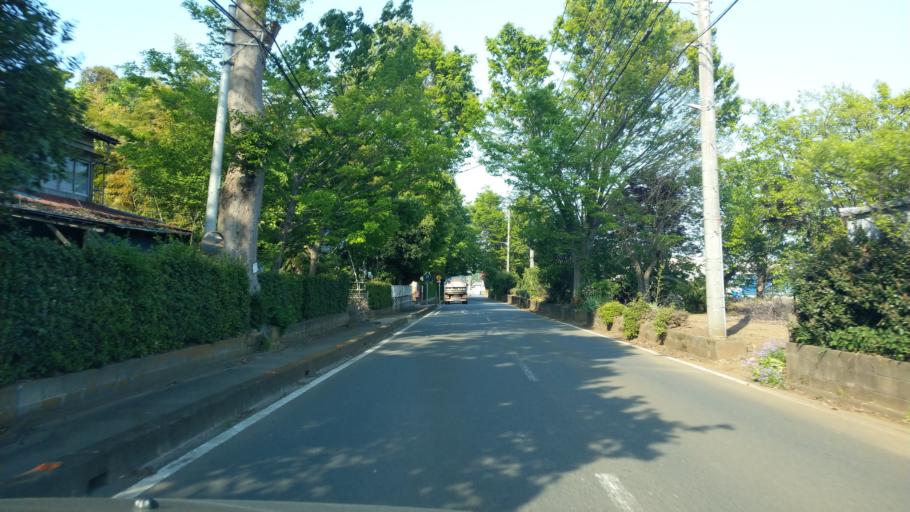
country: JP
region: Saitama
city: Oi
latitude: 35.8397
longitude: 139.4903
